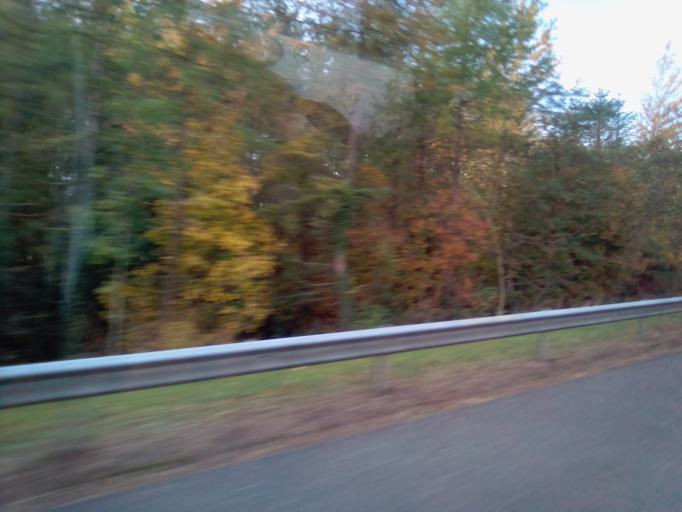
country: IE
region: Leinster
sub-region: Laois
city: Portlaoise
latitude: 53.0165
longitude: -7.3232
